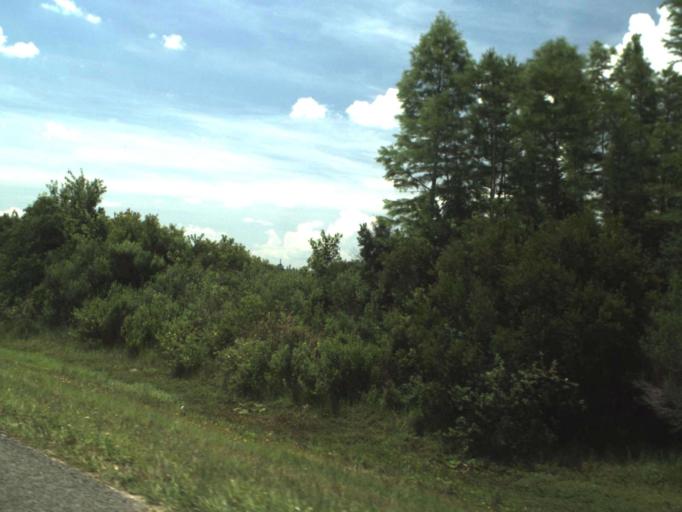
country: US
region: Florida
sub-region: Volusia County
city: Lake Helen
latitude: 29.0302
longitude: -81.1680
